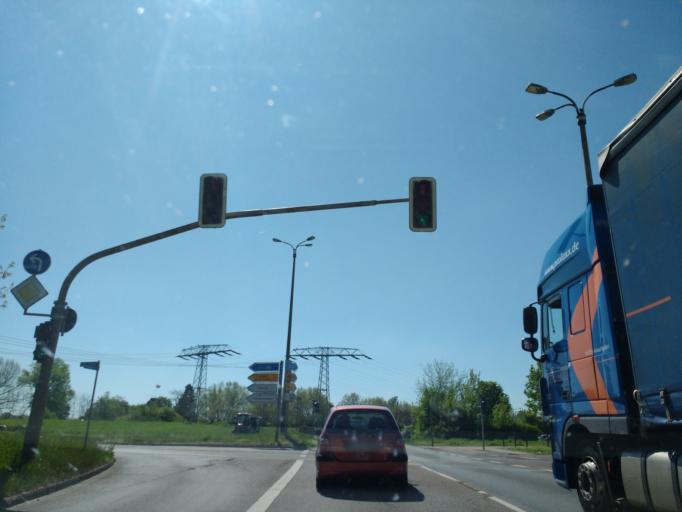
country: DE
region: Saxony-Anhalt
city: Halle Neustadt
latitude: 51.4808
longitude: 11.9446
